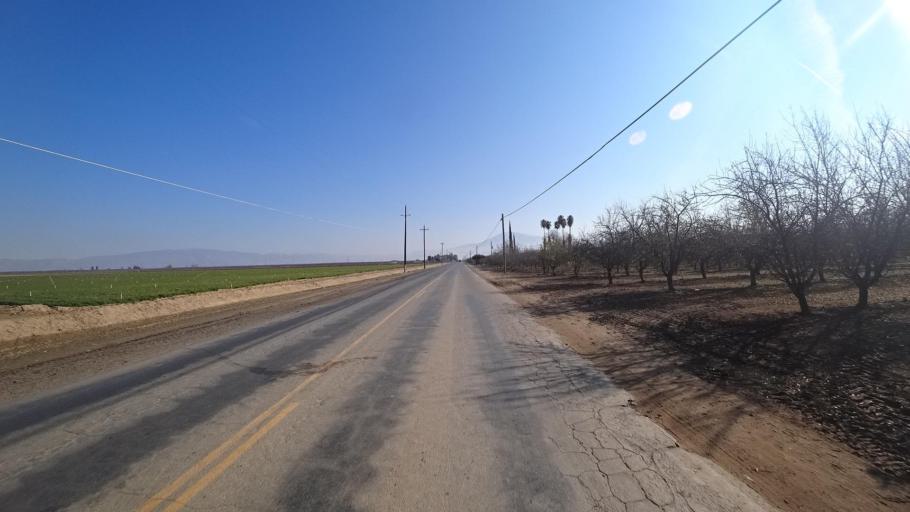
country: US
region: California
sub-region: Kern County
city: Weedpatch
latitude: 35.2380
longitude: -118.9094
